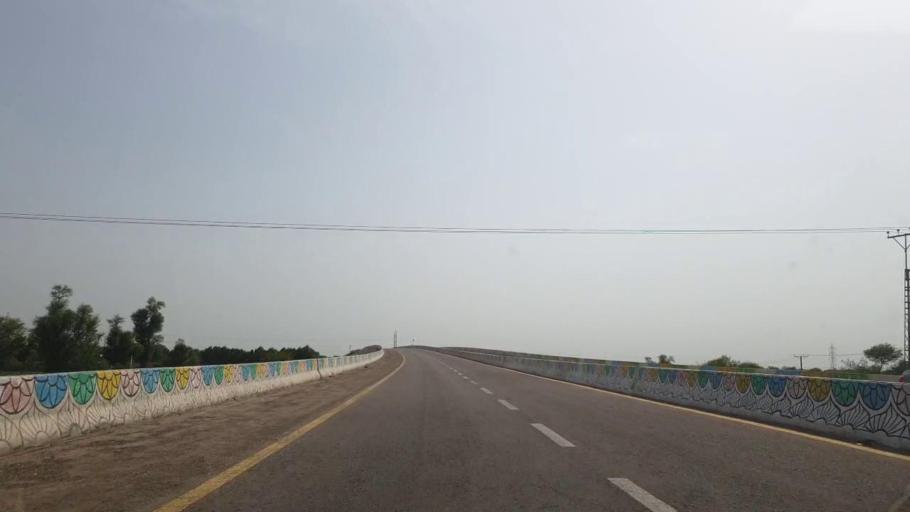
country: PK
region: Sindh
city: Sakrand
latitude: 26.1574
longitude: 68.2527
